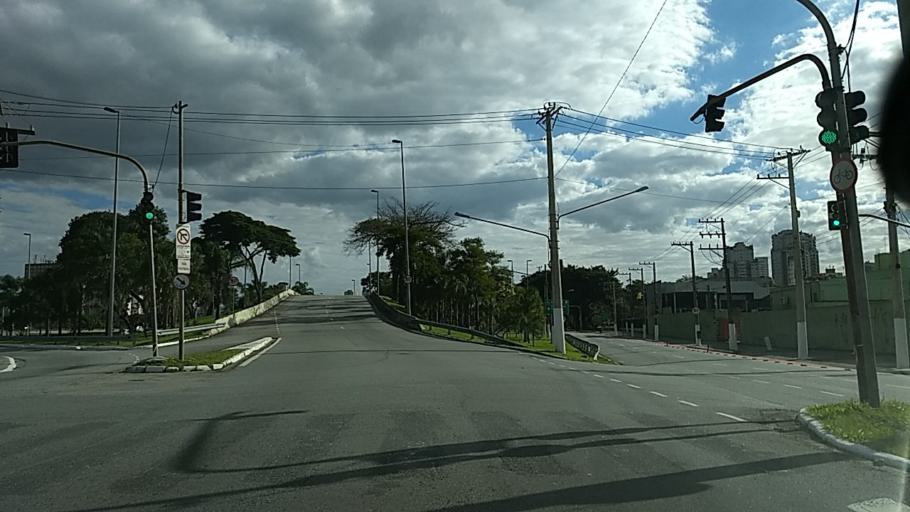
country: BR
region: Sao Paulo
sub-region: Sao Paulo
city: Sao Paulo
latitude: -23.5157
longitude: -46.6500
